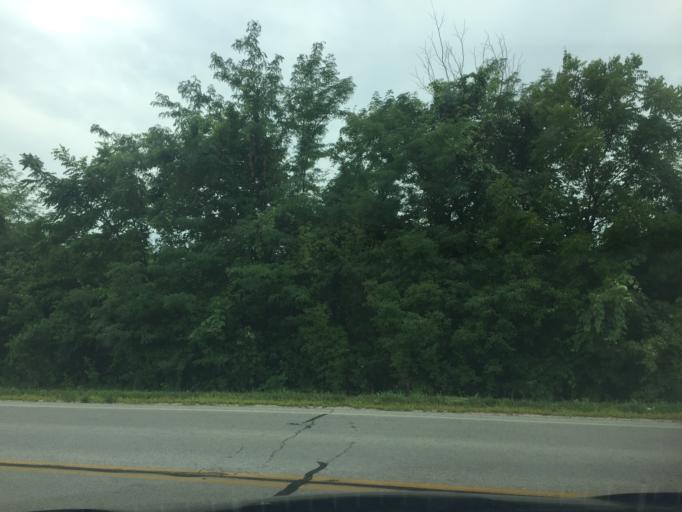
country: US
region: Missouri
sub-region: Platte County
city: Weston
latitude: 39.3698
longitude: -94.9393
